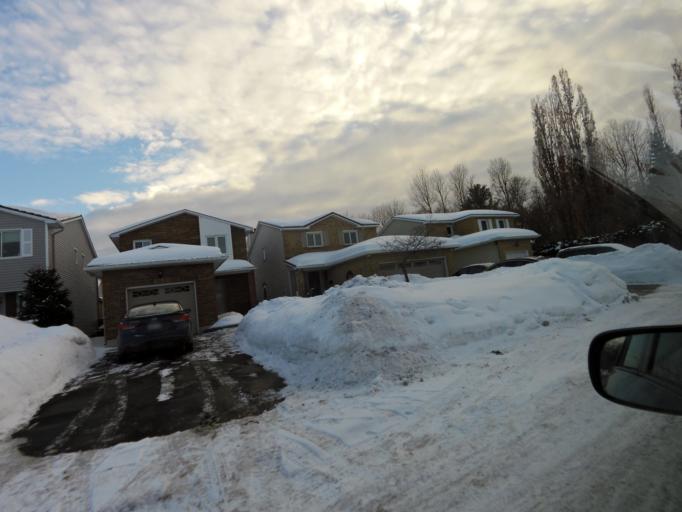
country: CA
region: Quebec
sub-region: Outaouais
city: Gatineau
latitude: 45.4571
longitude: -75.5440
